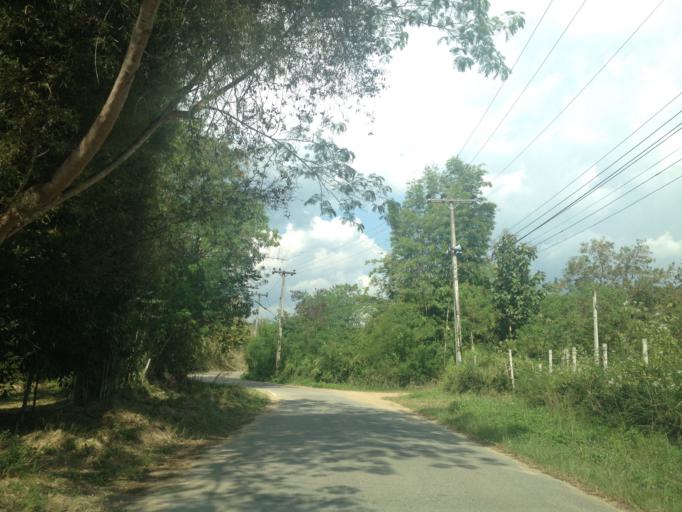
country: TH
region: Chiang Mai
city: Hang Dong
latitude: 18.7205
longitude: 98.8859
